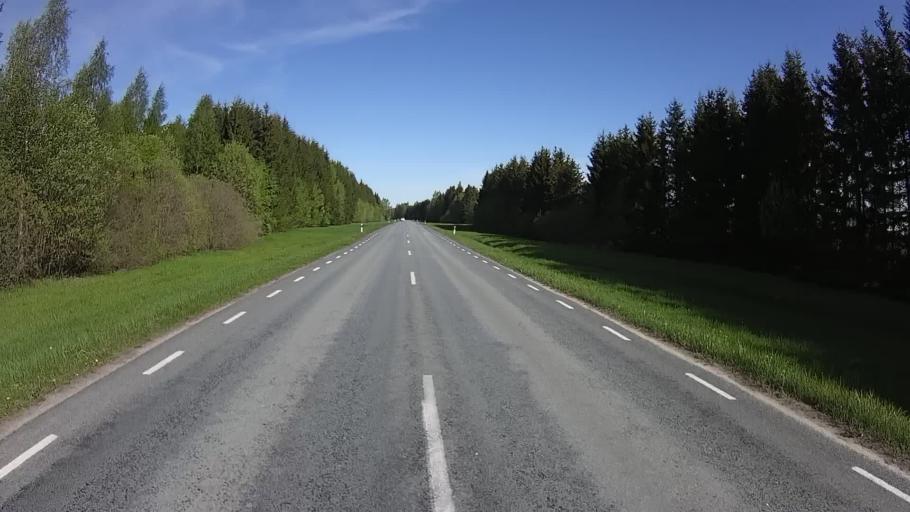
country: EE
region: Polvamaa
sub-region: Polva linn
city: Polva
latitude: 58.2299
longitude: 27.0237
